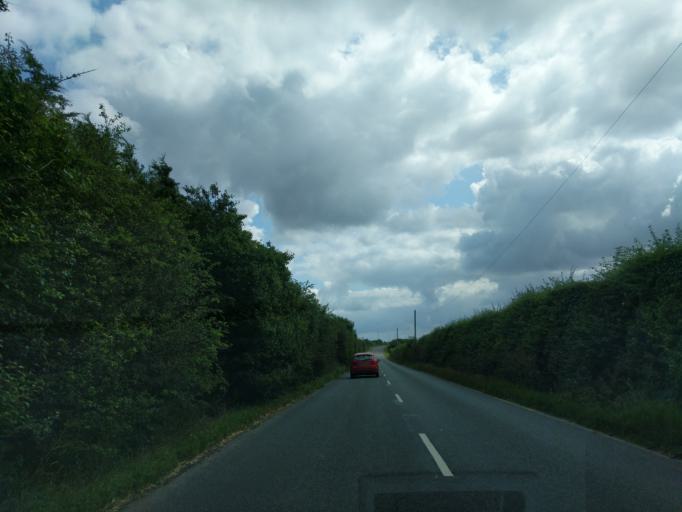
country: GB
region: England
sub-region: Cambridgeshire
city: Isleham
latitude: 52.2905
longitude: 0.4633
